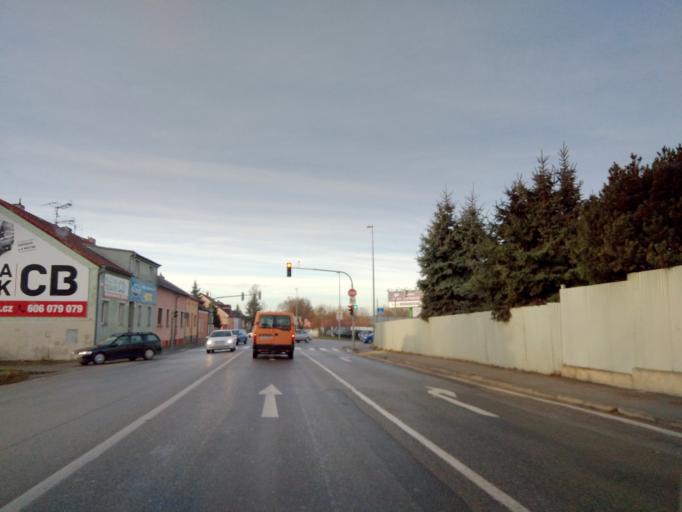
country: CZ
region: Jihocesky
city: Rudolfov
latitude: 48.9834
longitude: 14.5083
